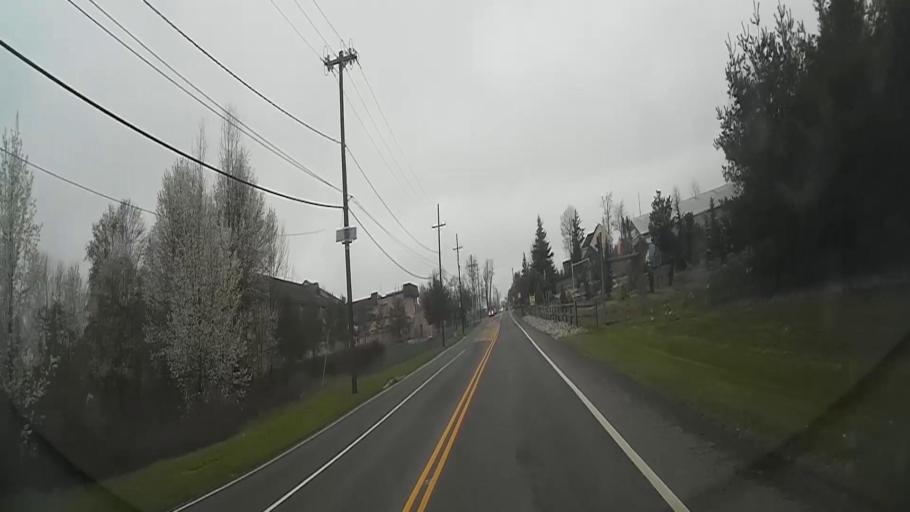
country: US
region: New Jersey
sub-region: Burlington County
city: Marlton
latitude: 39.8682
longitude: -74.8948
